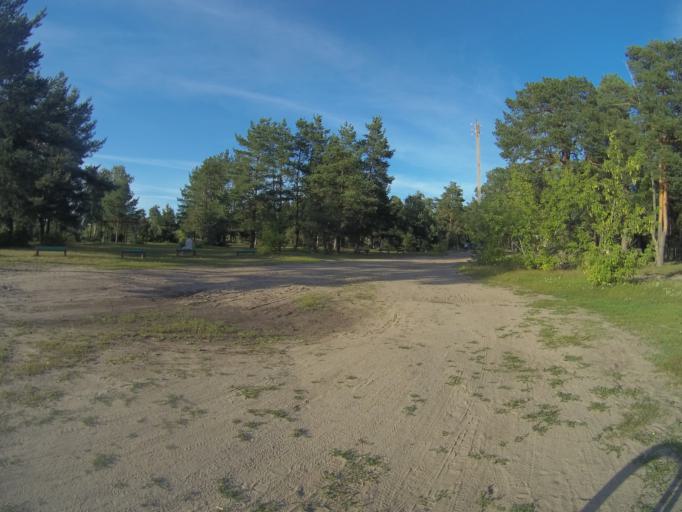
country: RU
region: Vladimir
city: Kommunar
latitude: 56.1002
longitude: 40.4367
